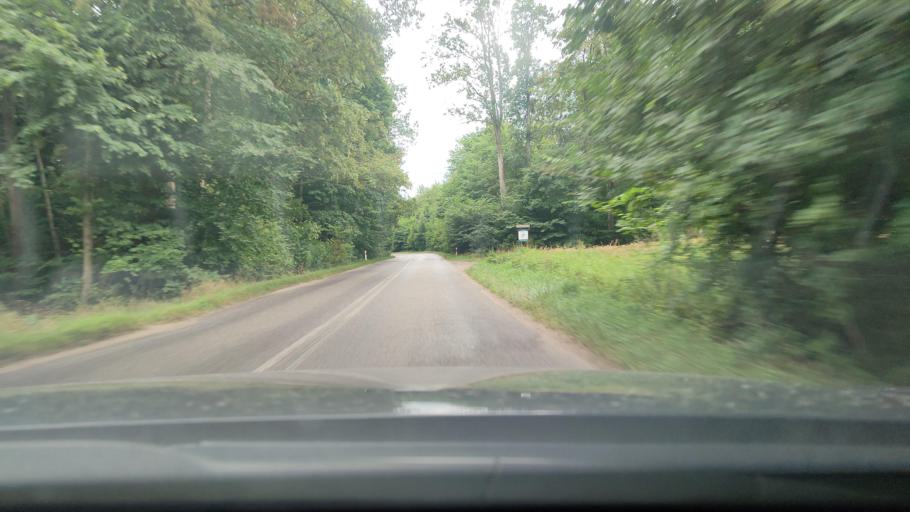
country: PL
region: Pomeranian Voivodeship
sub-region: Powiat pucki
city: Krokowa
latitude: 54.7662
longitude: 18.1647
